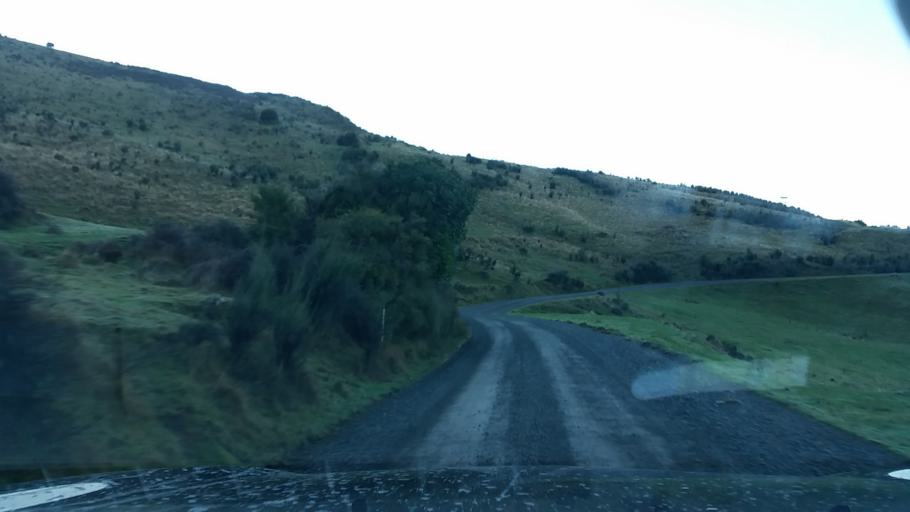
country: NZ
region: Marlborough
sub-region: Marlborough District
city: Blenheim
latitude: -41.7842
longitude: 173.7964
